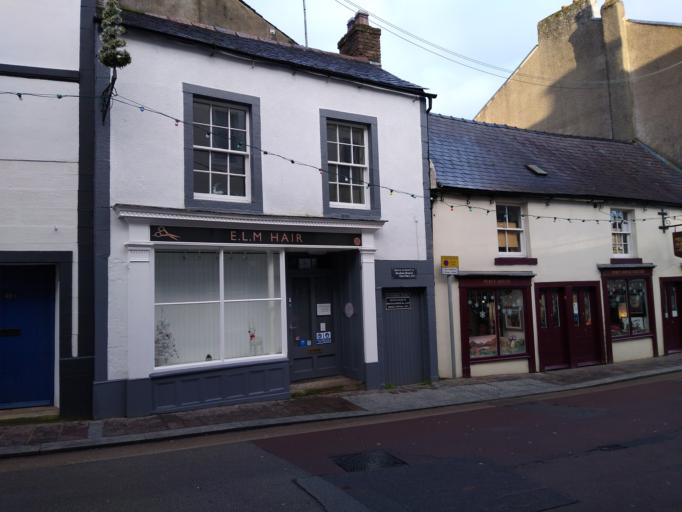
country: GB
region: England
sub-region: Cumbria
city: Cockermouth
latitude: 54.6641
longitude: -3.3619
